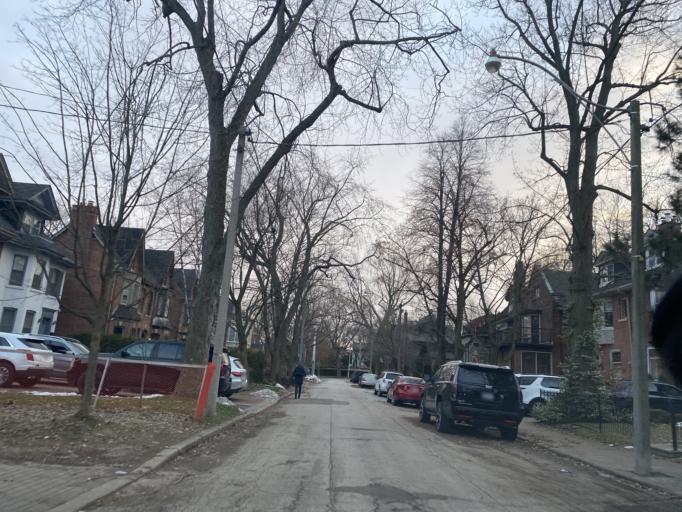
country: CA
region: Ontario
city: Toronto
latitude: 43.6756
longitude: -79.3718
